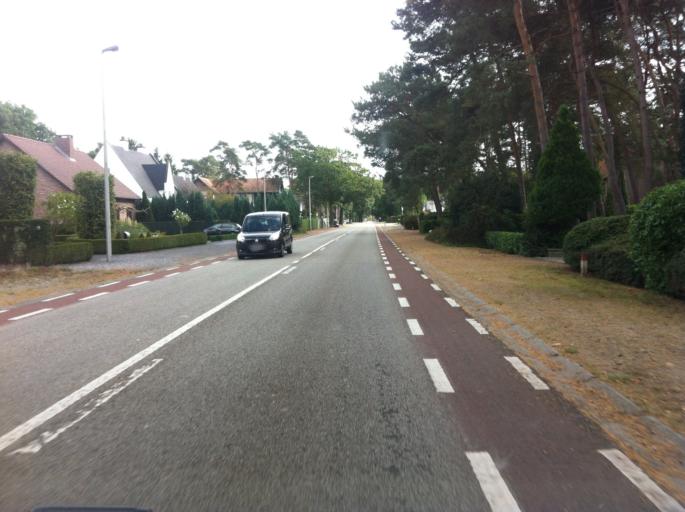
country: BE
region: Flanders
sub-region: Provincie Limburg
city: Maasmechelen
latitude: 50.9735
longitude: 5.6757
